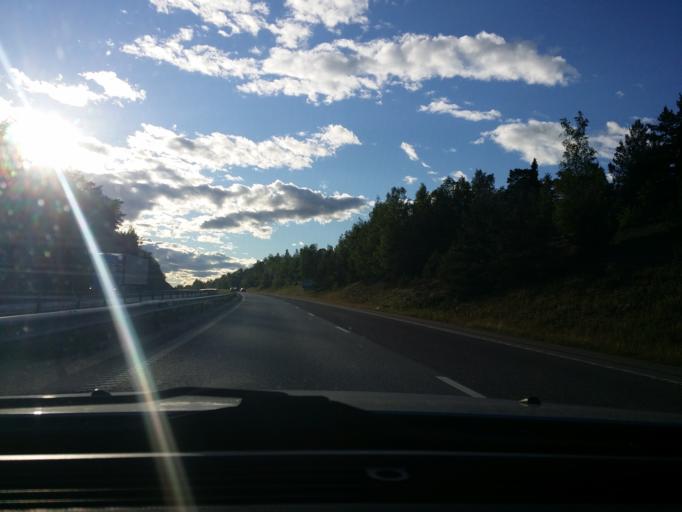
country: SE
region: Uppsala
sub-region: Habo Kommun
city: Balsta
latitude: 59.5764
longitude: 17.5407
